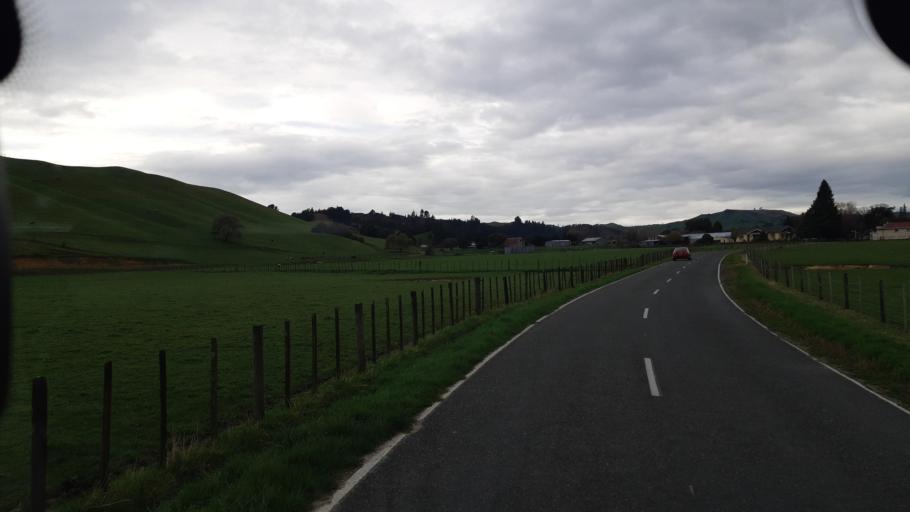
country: NZ
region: Tasman
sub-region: Tasman District
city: Motueka
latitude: -41.2755
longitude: 172.8718
